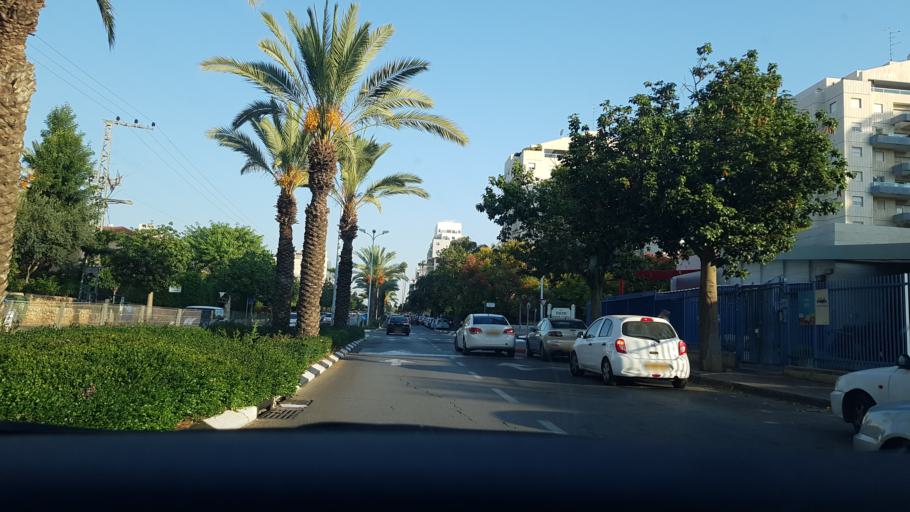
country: IL
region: Central District
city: Ness Ziona
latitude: 31.8986
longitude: 34.8203
